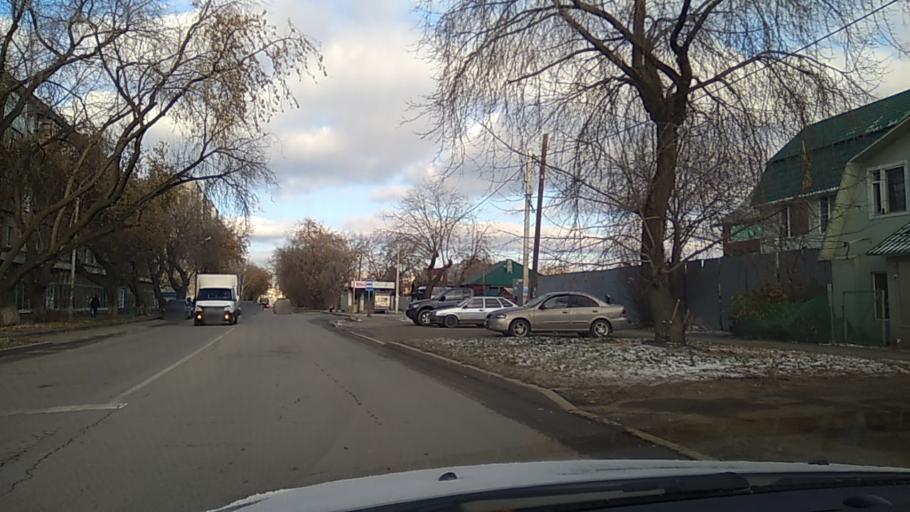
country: RU
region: Sverdlovsk
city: Sovkhoznyy
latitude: 56.7501
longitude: 60.6198
